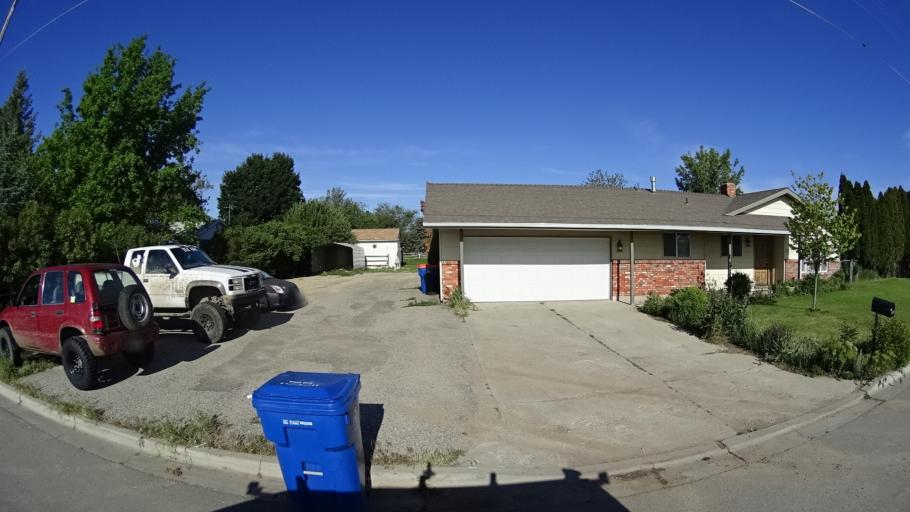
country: US
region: Idaho
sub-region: Ada County
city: Garden City
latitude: 43.5466
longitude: -116.2755
